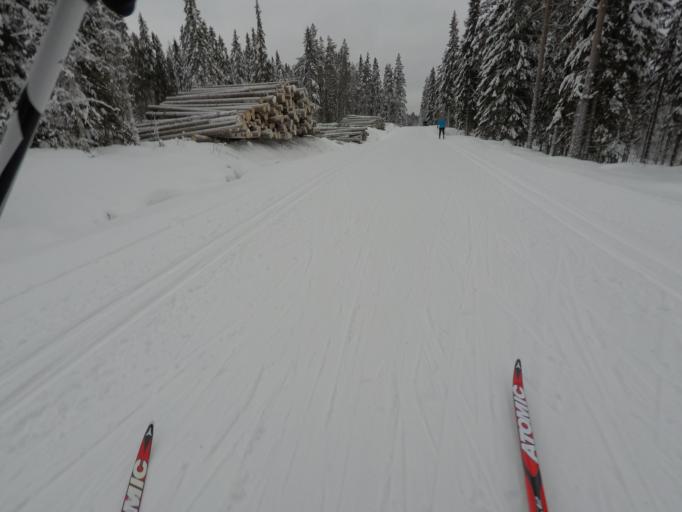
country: SE
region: Dalarna
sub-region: Ludvika Kommun
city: Abborrberget
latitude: 60.1585
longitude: 14.4892
